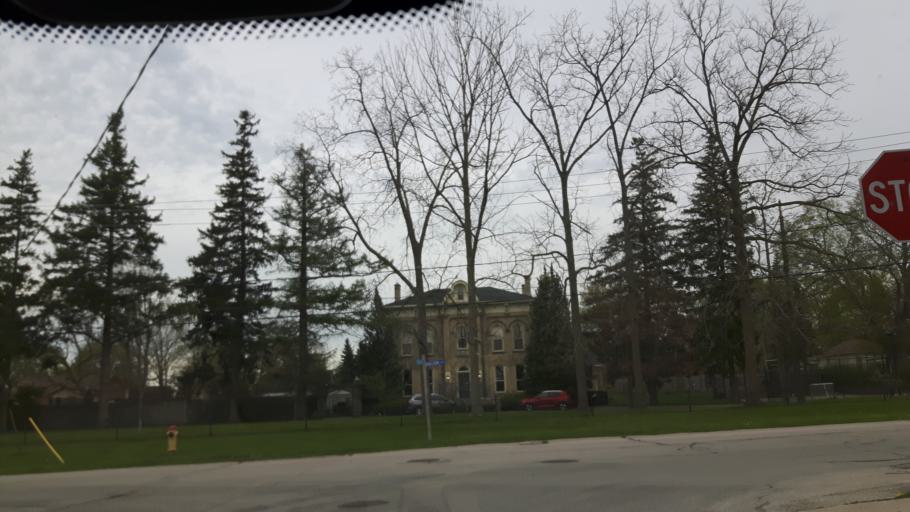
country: CA
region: Ontario
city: Goderich
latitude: 43.7454
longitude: -81.7125
